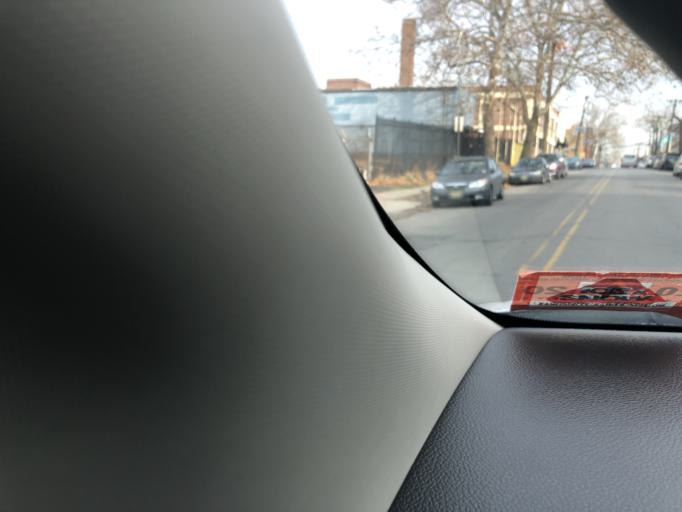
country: US
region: New Jersey
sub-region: Essex County
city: Irvington
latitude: 40.7188
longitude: -74.2258
